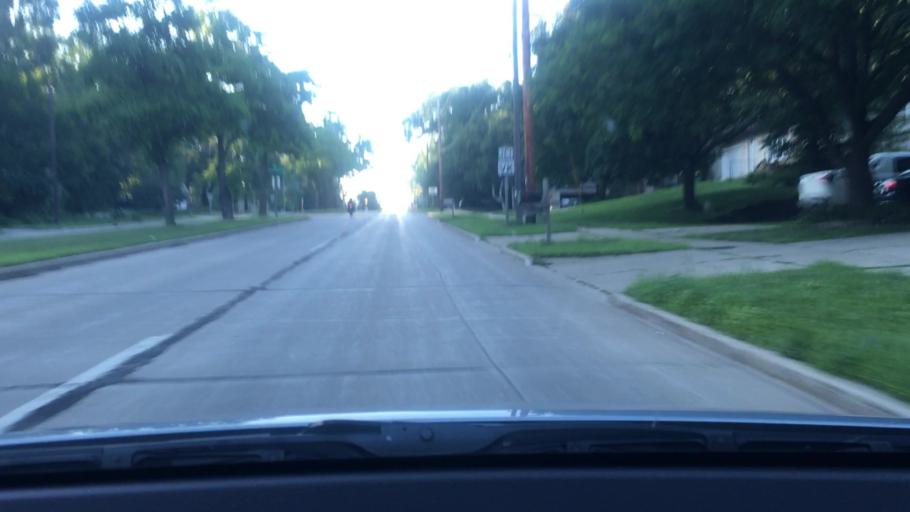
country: US
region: Wisconsin
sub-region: Brown County
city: Howard
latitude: 44.5077
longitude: -88.0992
